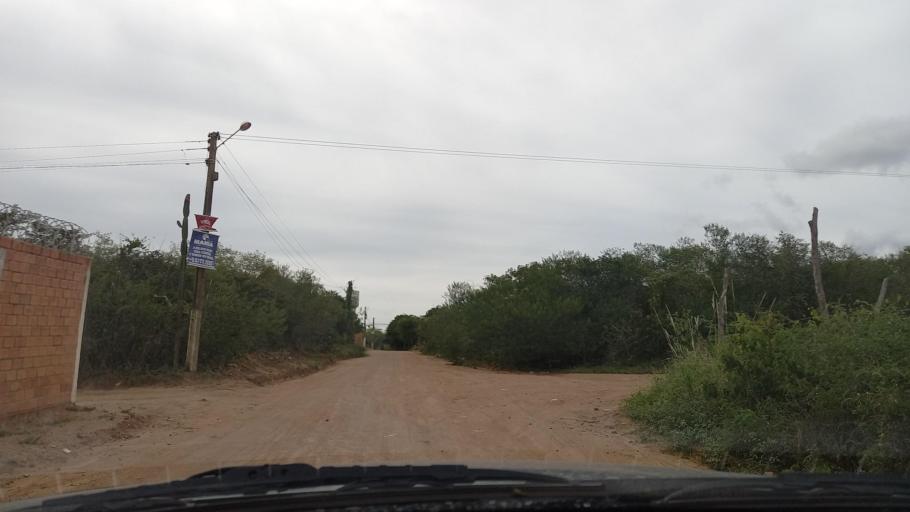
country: BR
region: Pernambuco
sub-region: Gravata
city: Gravata
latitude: -8.1966
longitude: -35.5913
